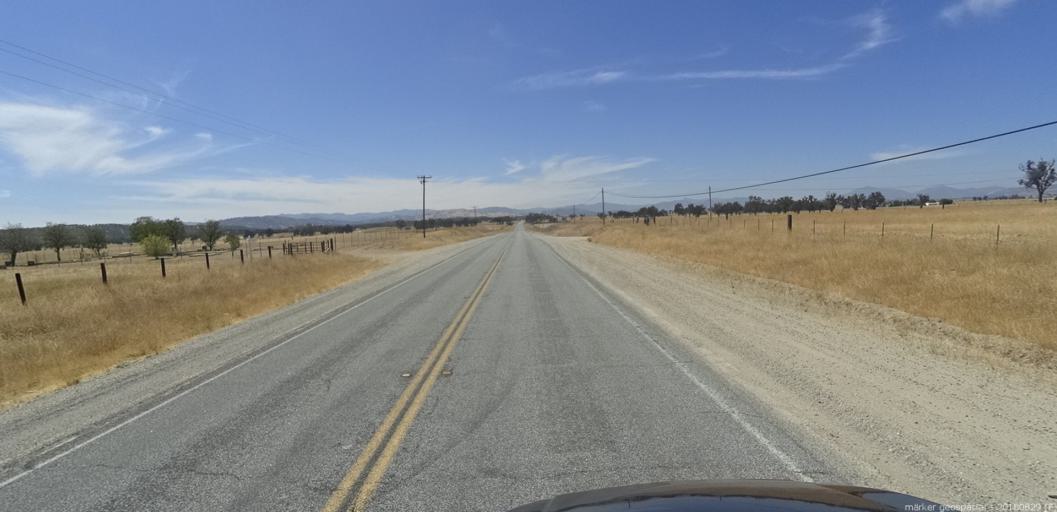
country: US
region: California
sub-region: Monterey County
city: King City
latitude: 35.9367
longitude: -121.0720
